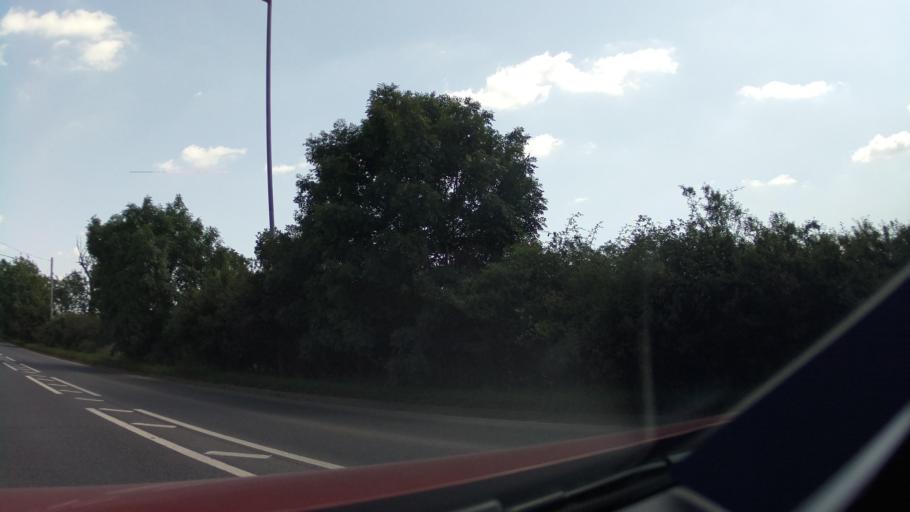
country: GB
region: England
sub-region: Warwickshire
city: Nuneaton
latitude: 52.5437
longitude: -1.4384
